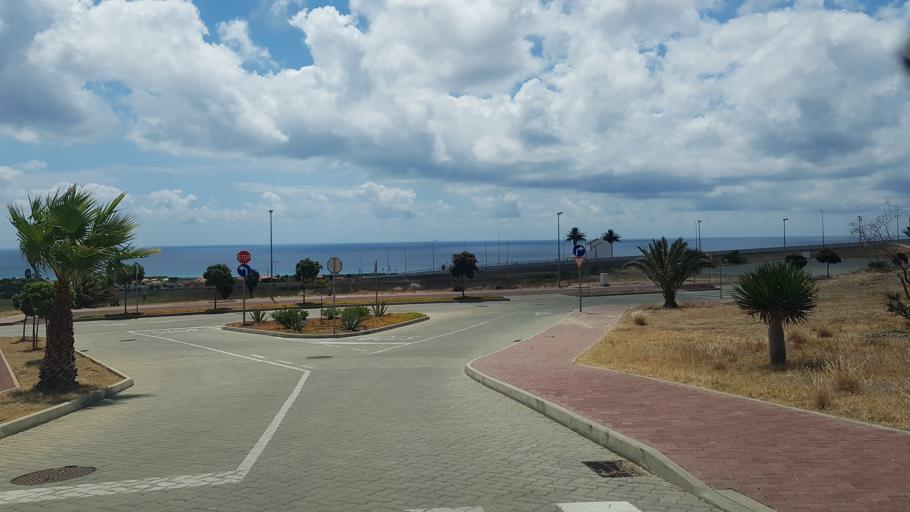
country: PT
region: Madeira
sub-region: Porto Santo
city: Vila de Porto Santo
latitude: 33.0473
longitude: -16.3638
